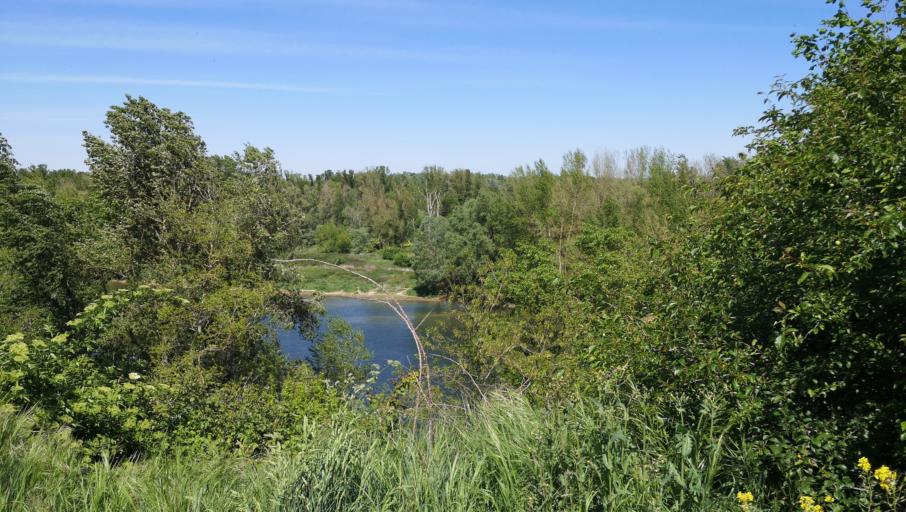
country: FR
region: Midi-Pyrenees
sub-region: Departement de la Haute-Garonne
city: Beauzelle
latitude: 43.6726
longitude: 1.3759
